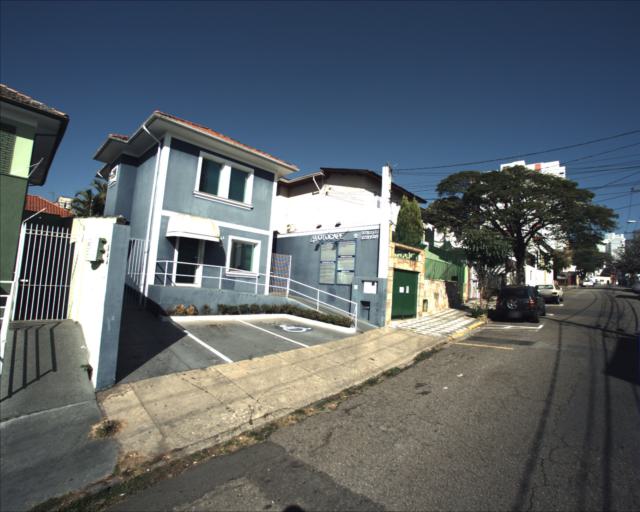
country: BR
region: Sao Paulo
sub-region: Sorocaba
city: Sorocaba
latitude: -23.5039
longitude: -47.4546
